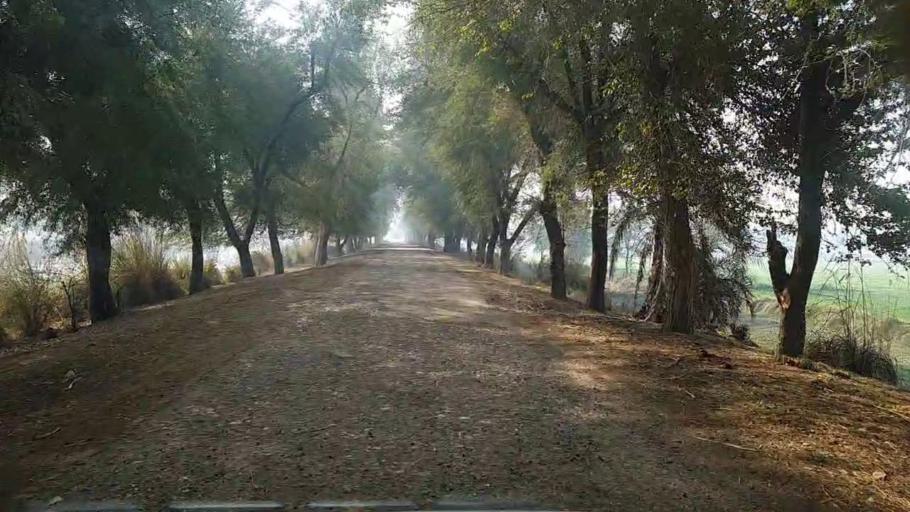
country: PK
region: Sindh
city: Khairpur
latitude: 27.9540
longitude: 69.6530
